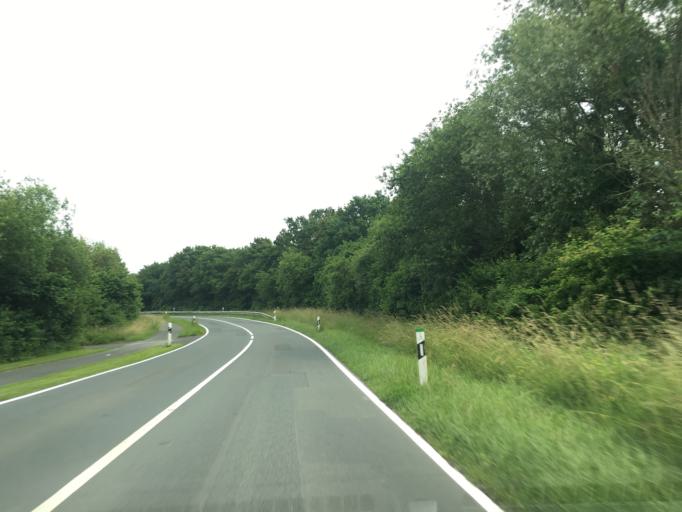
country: DE
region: North Rhine-Westphalia
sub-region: Regierungsbezirk Munster
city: Laer
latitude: 52.1000
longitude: 7.3925
